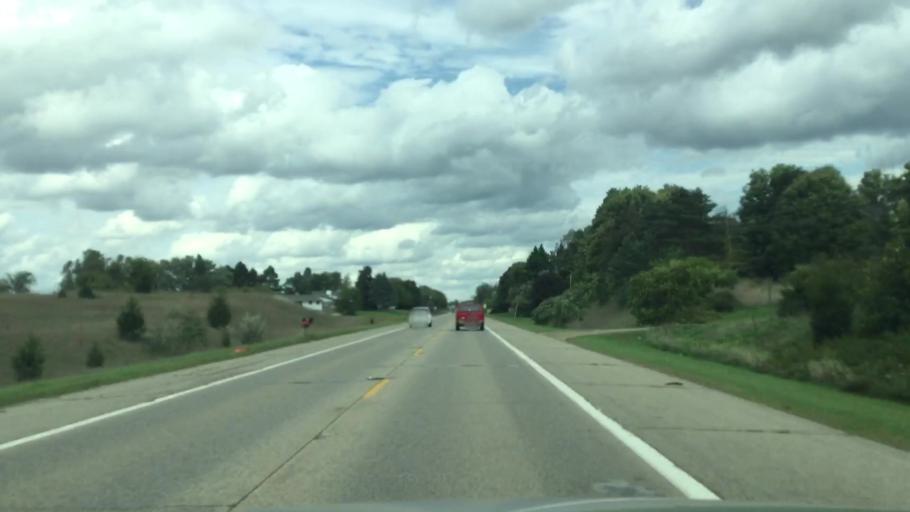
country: US
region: Michigan
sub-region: Shiawassee County
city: Owosso
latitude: 42.9610
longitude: -84.2034
